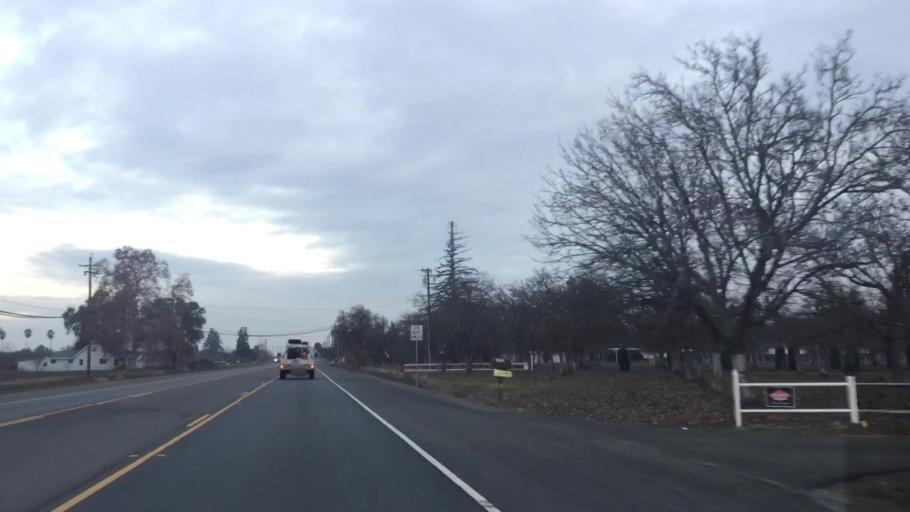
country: US
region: California
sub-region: Yuba County
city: Marysville
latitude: 39.2107
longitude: -121.5976
